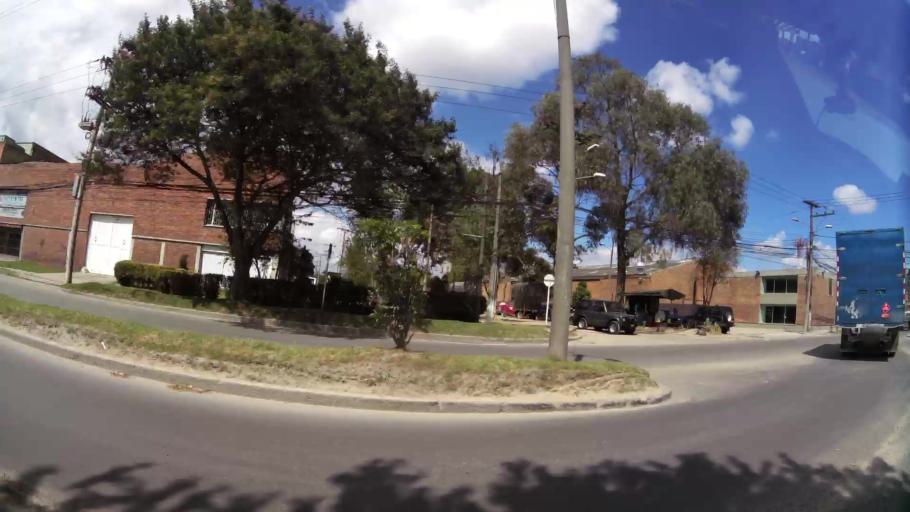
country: CO
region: Bogota D.C.
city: Bogota
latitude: 4.6344
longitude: -74.1109
